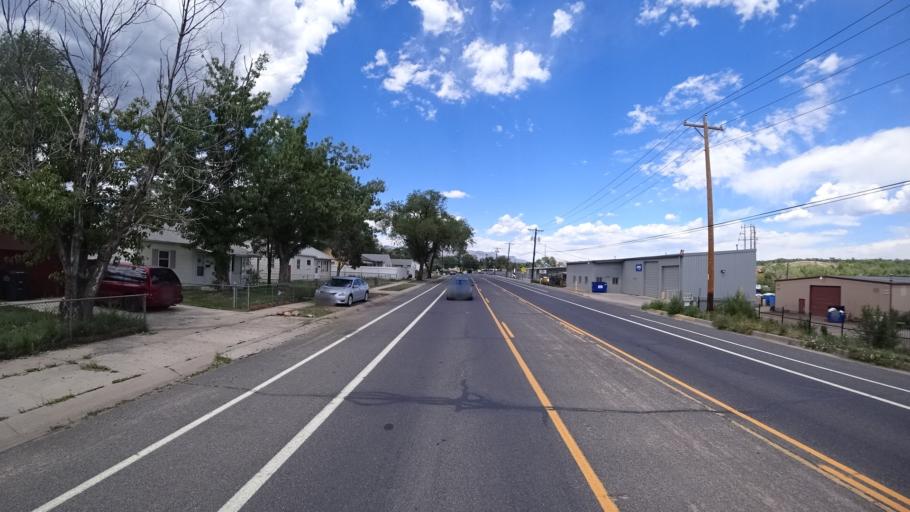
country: US
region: Colorado
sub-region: El Paso County
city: Colorado Springs
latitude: 38.8051
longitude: -104.8047
